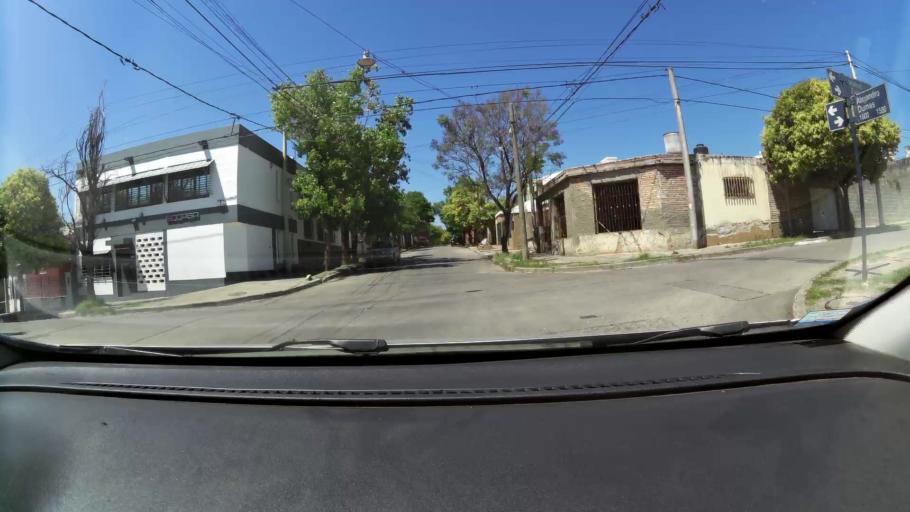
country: AR
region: Cordoba
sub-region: Departamento de Capital
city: Cordoba
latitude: -31.4311
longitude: -64.2078
